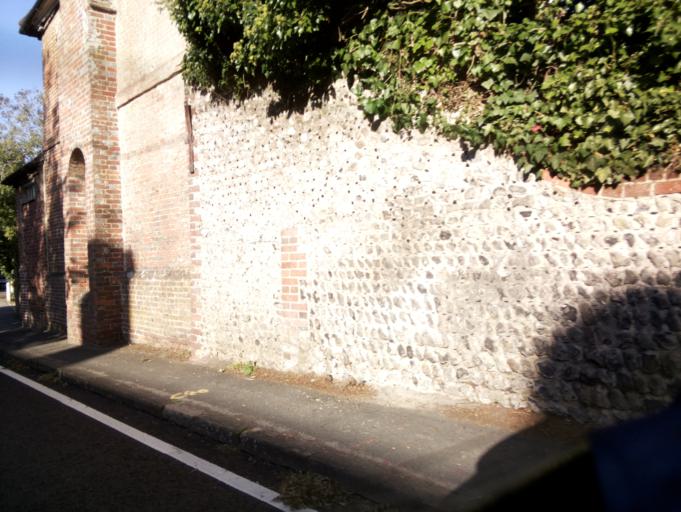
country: GB
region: England
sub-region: Hampshire
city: Swanmore
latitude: 50.9787
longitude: -1.1322
